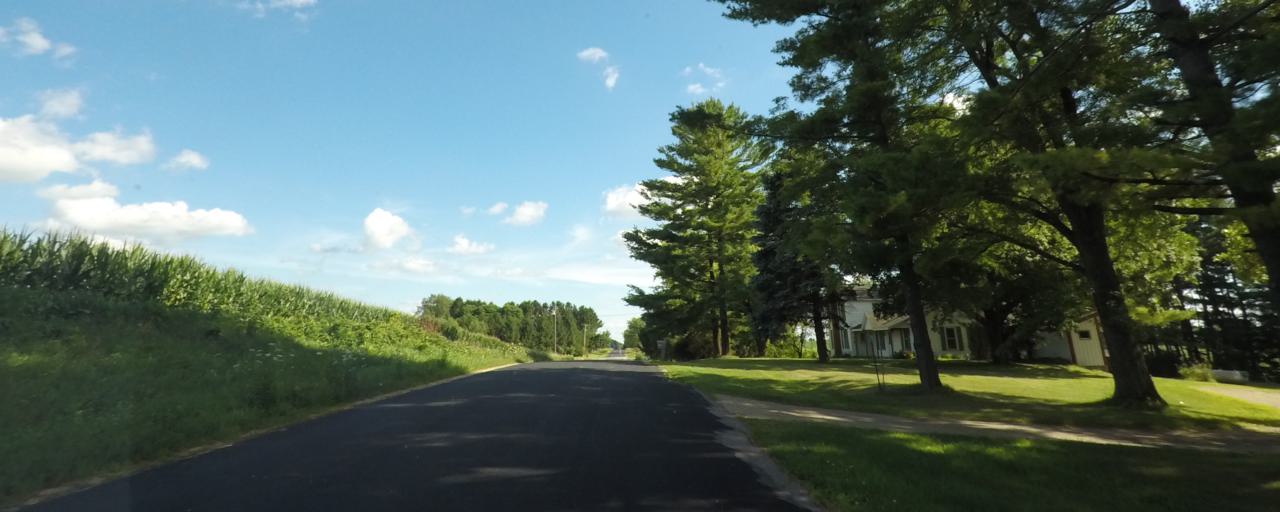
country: US
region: Wisconsin
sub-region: Rock County
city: Edgerton
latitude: 42.8635
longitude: -89.1320
